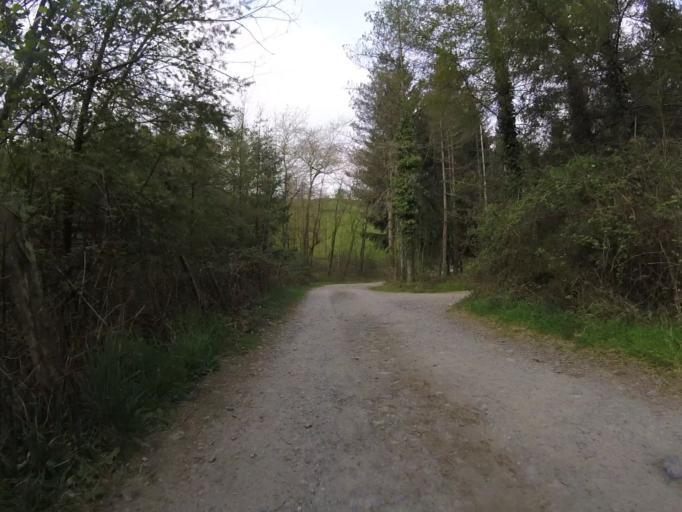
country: ES
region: Navarre
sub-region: Provincia de Navarra
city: Areso
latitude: 43.1069
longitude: -1.9555
